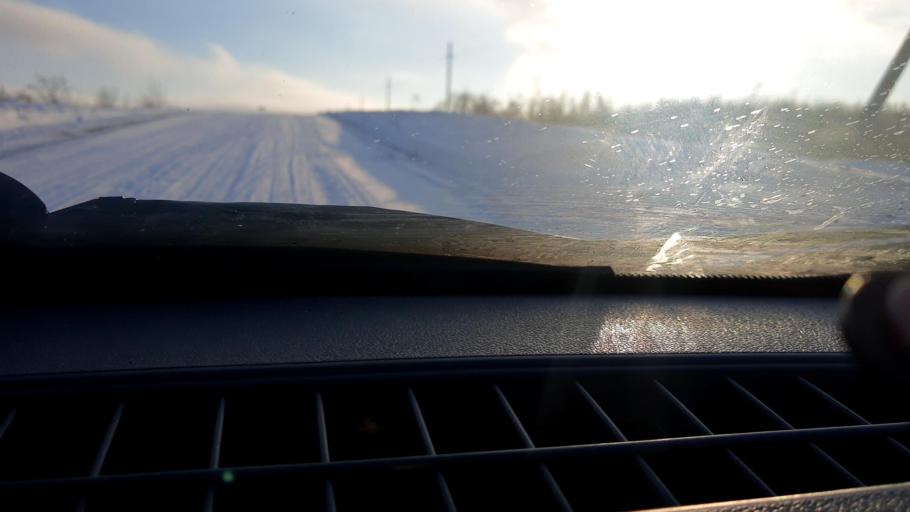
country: RU
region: Bashkortostan
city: Kushnarenkovo
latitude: 55.1336
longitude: 55.6155
